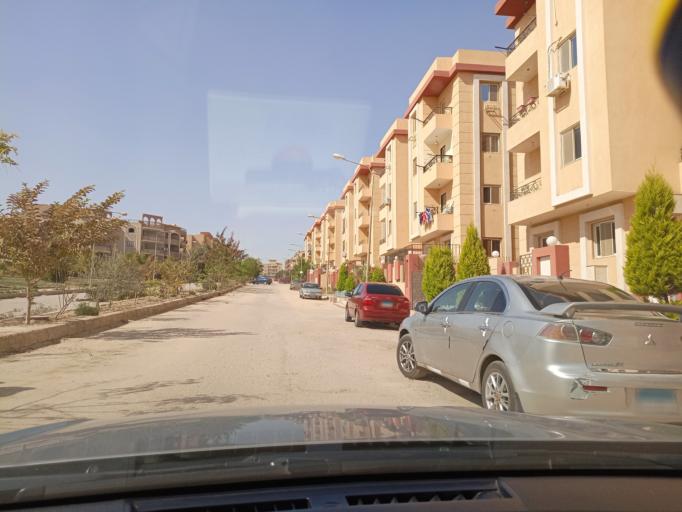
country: EG
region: Muhafazat al Qalyubiyah
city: Al Khankah
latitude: 30.2167
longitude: 31.4430
